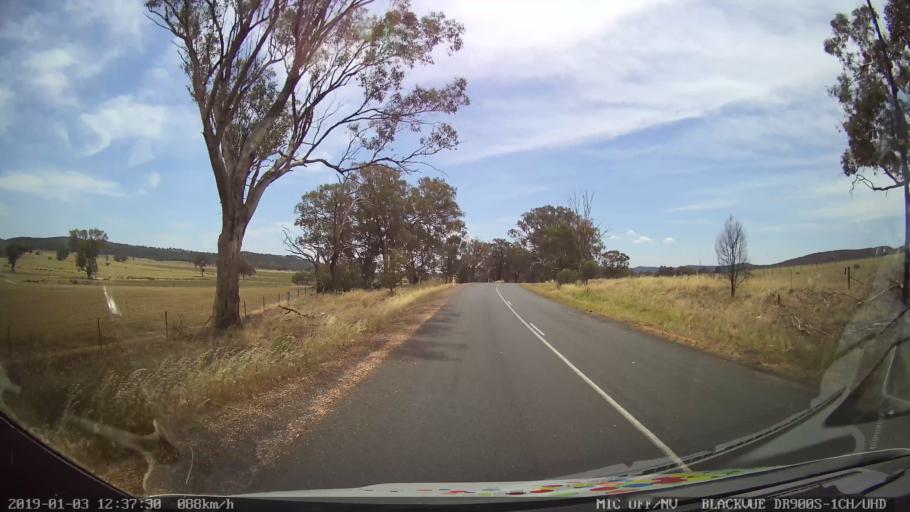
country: AU
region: New South Wales
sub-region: Weddin
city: Grenfell
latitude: -33.8418
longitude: 148.1851
